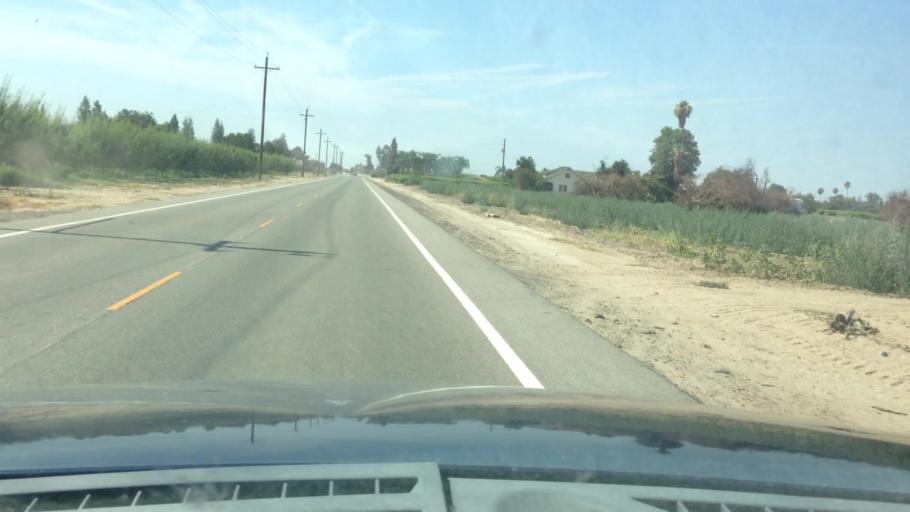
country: US
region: California
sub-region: Fresno County
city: Parlier
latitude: 36.5745
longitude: -119.5571
